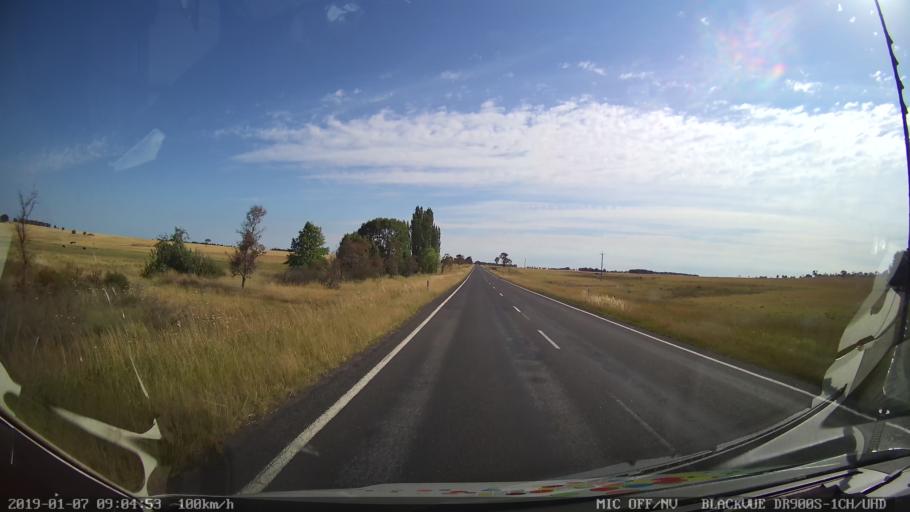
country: AU
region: New South Wales
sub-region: Armidale Dumaresq
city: Armidale
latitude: -30.7161
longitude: 151.4569
